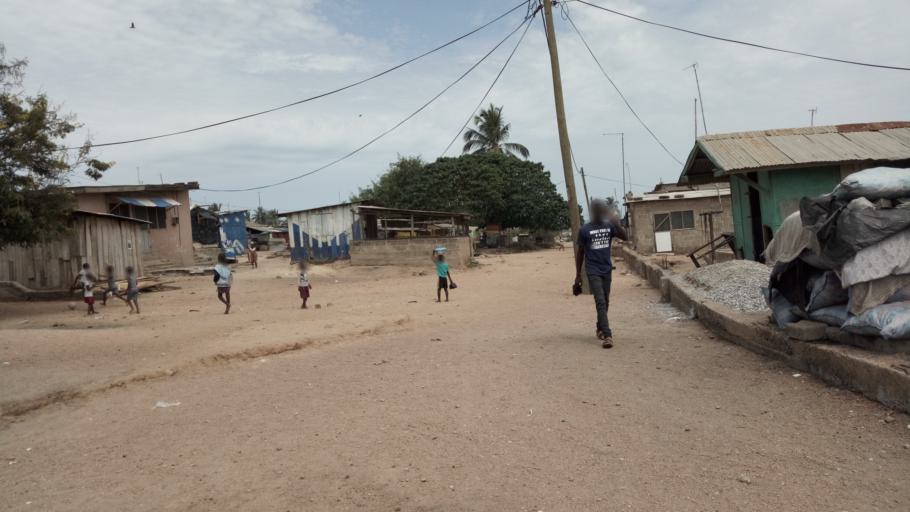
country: GH
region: Central
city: Winneba
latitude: 5.3496
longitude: -0.6158
